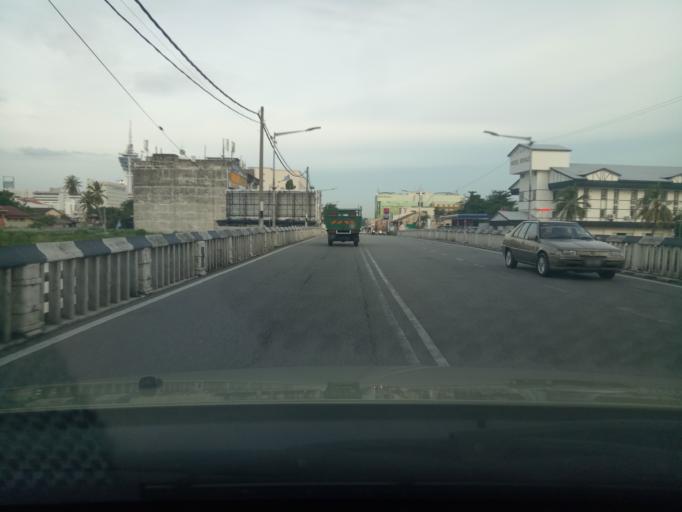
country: MY
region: Kedah
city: Alor Setar
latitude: 6.1243
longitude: 100.3595
